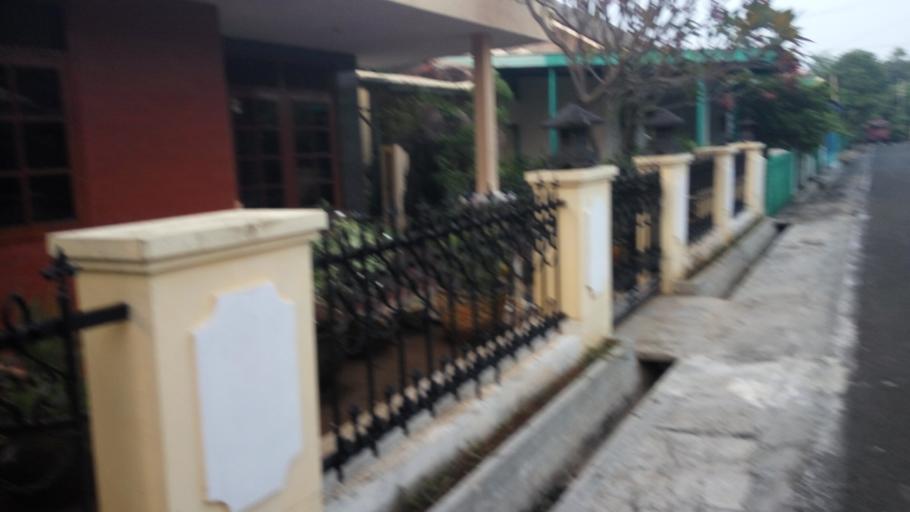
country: ID
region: Central Java
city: Semarang
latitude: -6.9880
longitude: 110.4054
